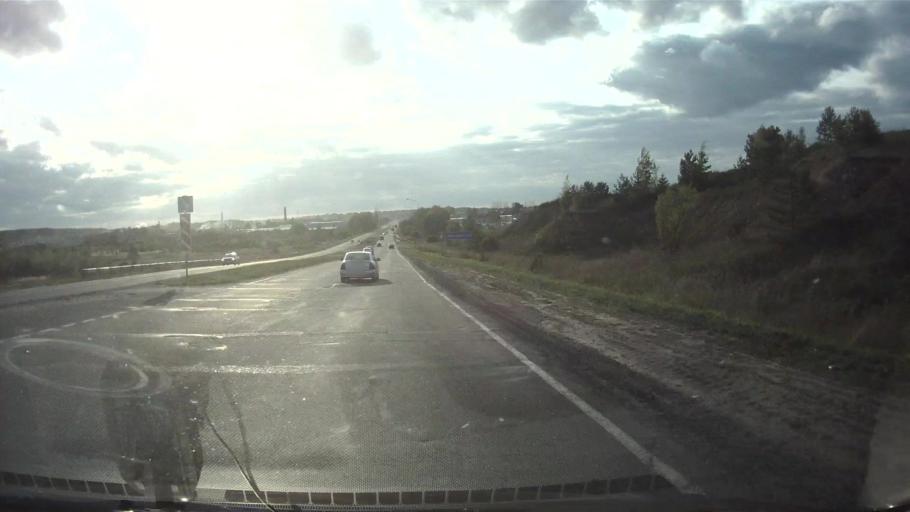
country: RU
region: Mariy-El
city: Sovetskiy
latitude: 56.7531
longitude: 48.4984
